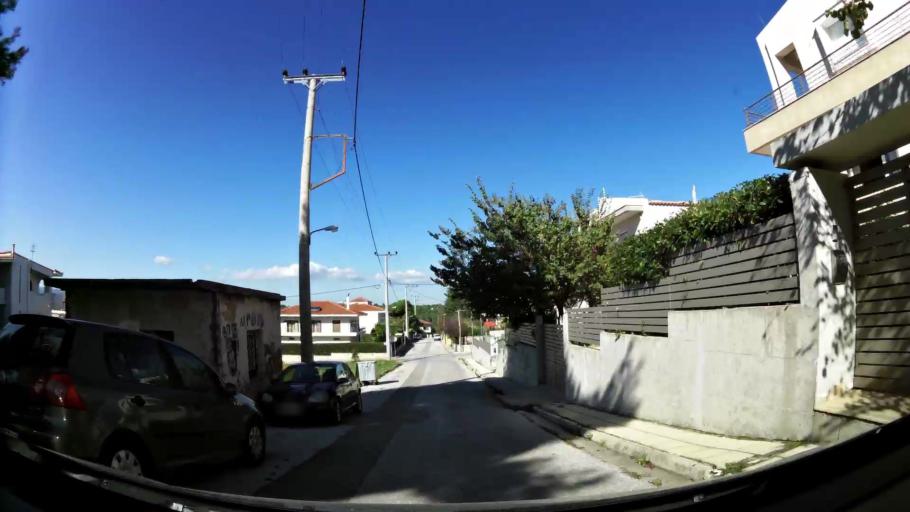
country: GR
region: Attica
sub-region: Nomarchia Anatolikis Attikis
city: Rodopoli
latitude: 38.1184
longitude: 23.8758
